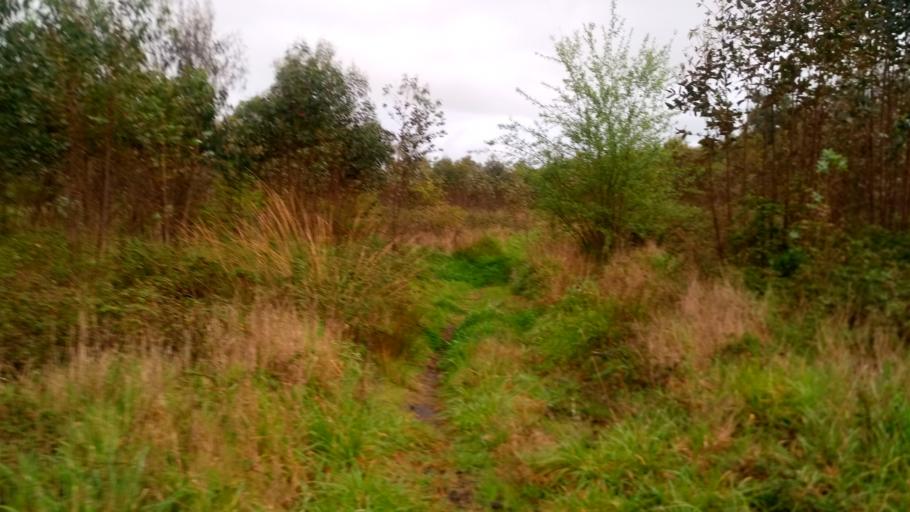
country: PT
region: Leiria
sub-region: Caldas da Rainha
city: Caldas da Rainha
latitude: 39.4317
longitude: -9.1671
